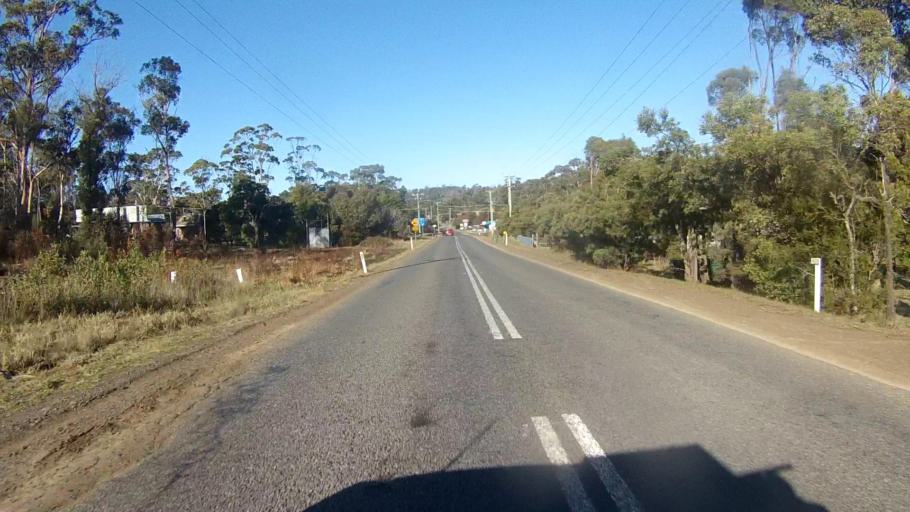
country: AU
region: Tasmania
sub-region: Sorell
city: Sorell
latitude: -42.9433
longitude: 147.8646
